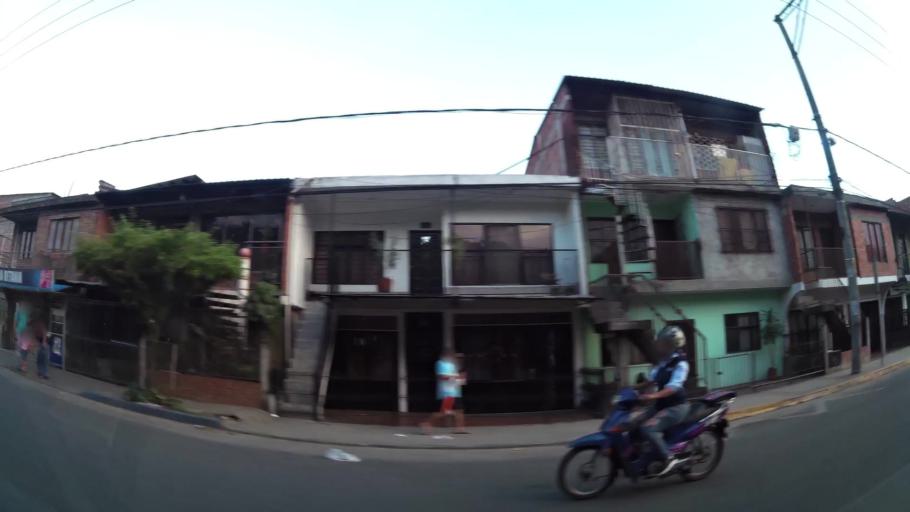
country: CO
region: Valle del Cauca
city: Cali
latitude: 3.4120
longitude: -76.4916
